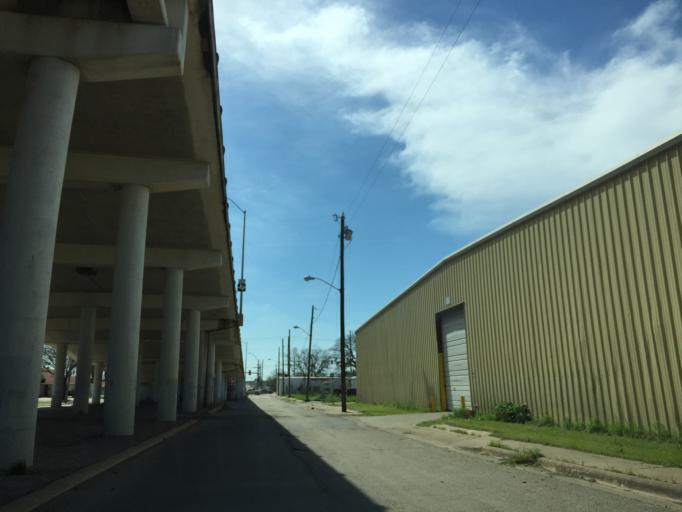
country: US
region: Texas
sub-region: Williamson County
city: Taylor
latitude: 30.5662
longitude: -97.4093
